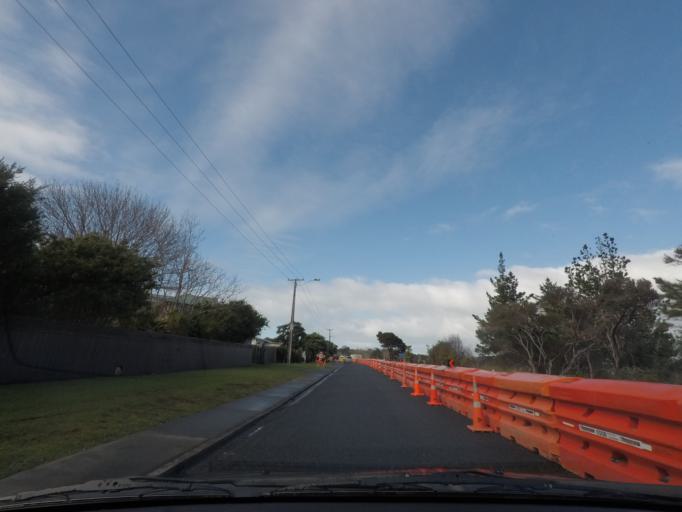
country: NZ
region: Auckland
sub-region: Auckland
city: Warkworth
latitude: -36.4331
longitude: 174.7385
